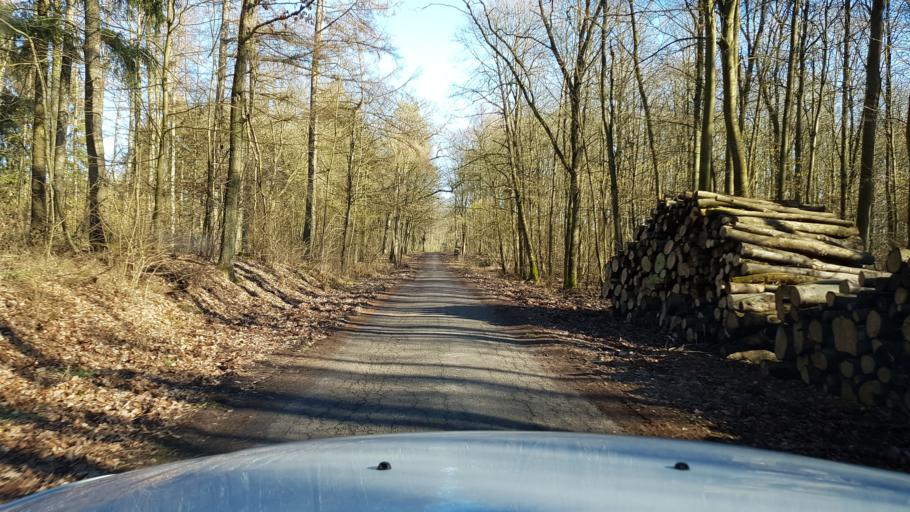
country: PL
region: West Pomeranian Voivodeship
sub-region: Powiat pyrzycki
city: Lipiany
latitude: 53.0354
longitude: 15.0332
